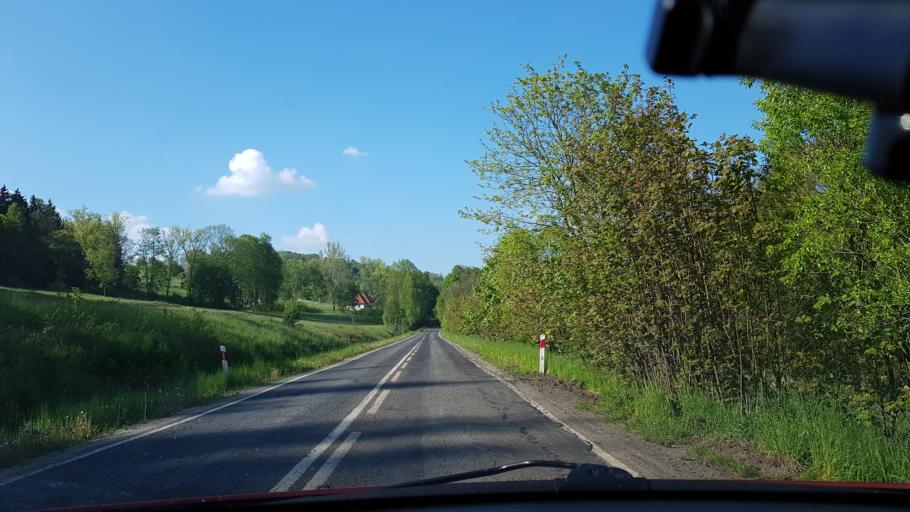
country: PL
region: Lower Silesian Voivodeship
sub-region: Powiat klodzki
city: Nowa Ruda
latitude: 50.5583
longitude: 16.4671
